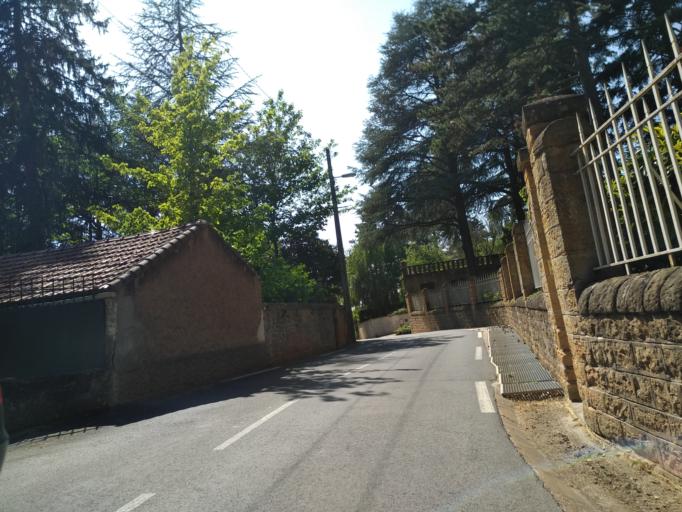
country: FR
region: Rhone-Alpes
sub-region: Departement du Rhone
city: Fontaines-sur-Saone
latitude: 45.8186
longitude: 4.8213
